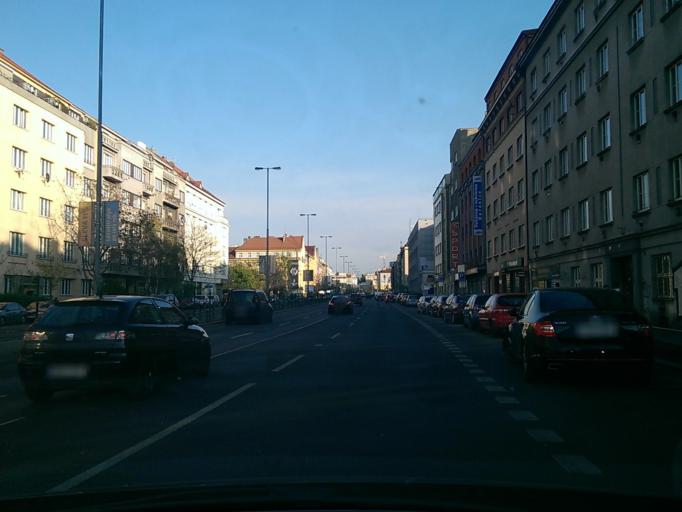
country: CZ
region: Praha
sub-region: Praha 2
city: Vysehrad
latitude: 50.0610
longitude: 14.4312
